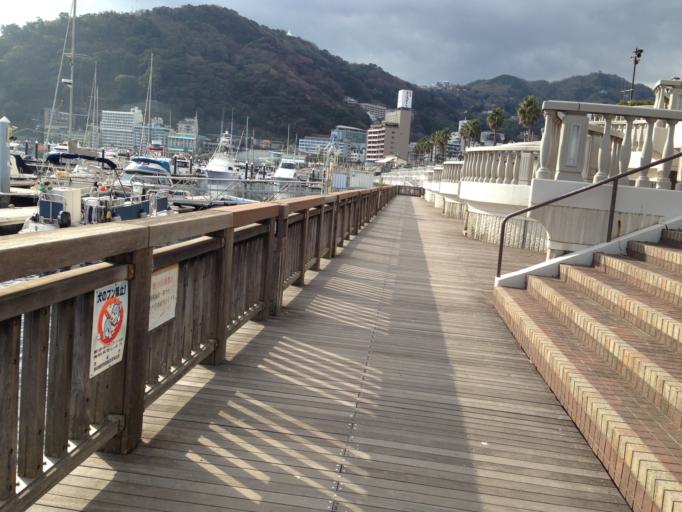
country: JP
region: Shizuoka
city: Atami
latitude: 35.0956
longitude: 139.0761
